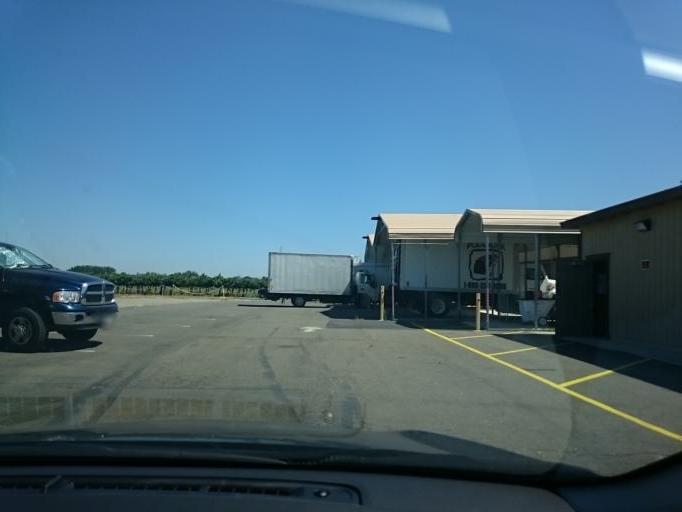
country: US
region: California
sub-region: Sacramento County
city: Parkway
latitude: 38.4604
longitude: -121.5063
